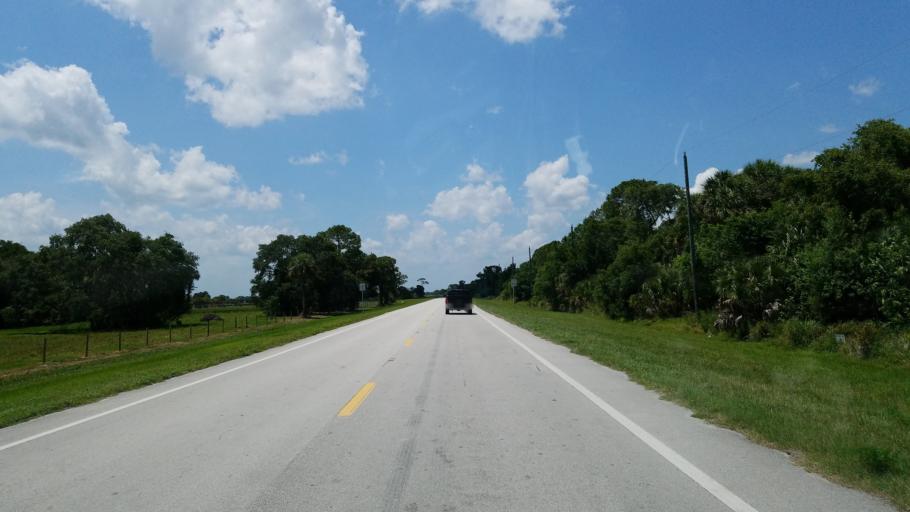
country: US
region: Florida
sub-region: Okeechobee County
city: Okeechobee
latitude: 27.2772
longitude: -80.8746
